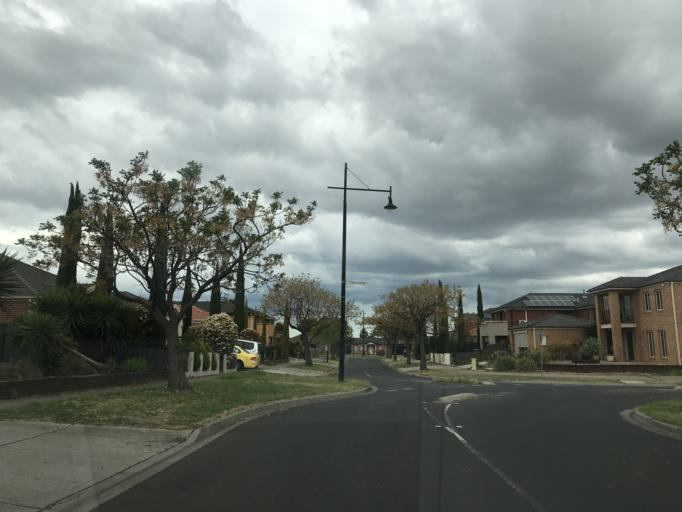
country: AU
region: Victoria
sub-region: Brimbank
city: Derrimut
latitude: -37.7954
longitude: 144.7655
